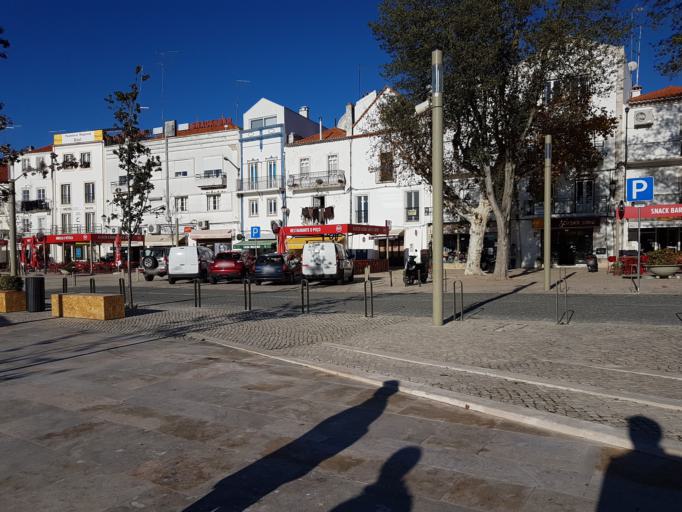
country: PT
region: Setubal
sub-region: Alcacer do Sal
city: Alcacer do Sal
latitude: 38.3706
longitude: -8.5066
